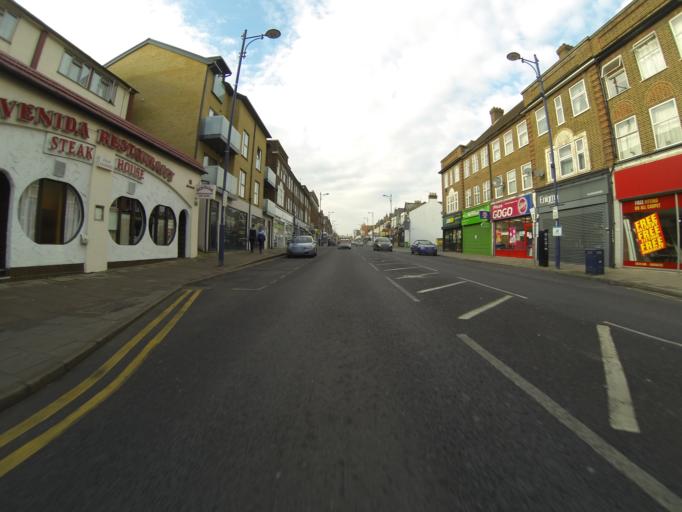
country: GB
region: England
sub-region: Greater London
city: Welling
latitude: 51.4632
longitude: 0.1030
